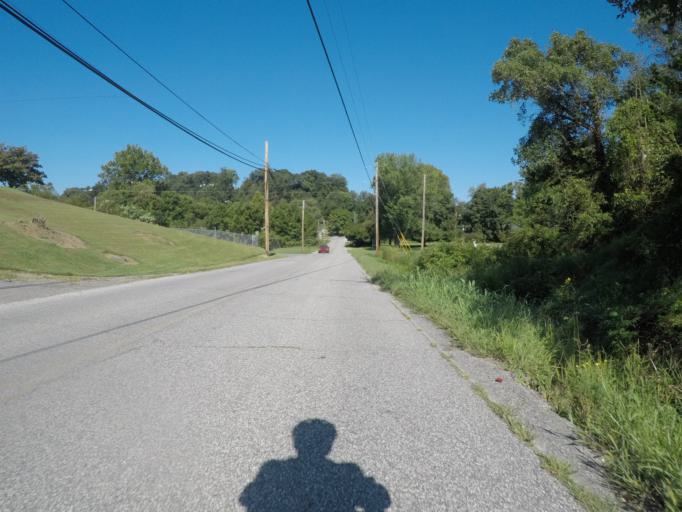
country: US
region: Kentucky
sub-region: Boyd County
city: Westwood
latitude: 38.4835
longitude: -82.6619
